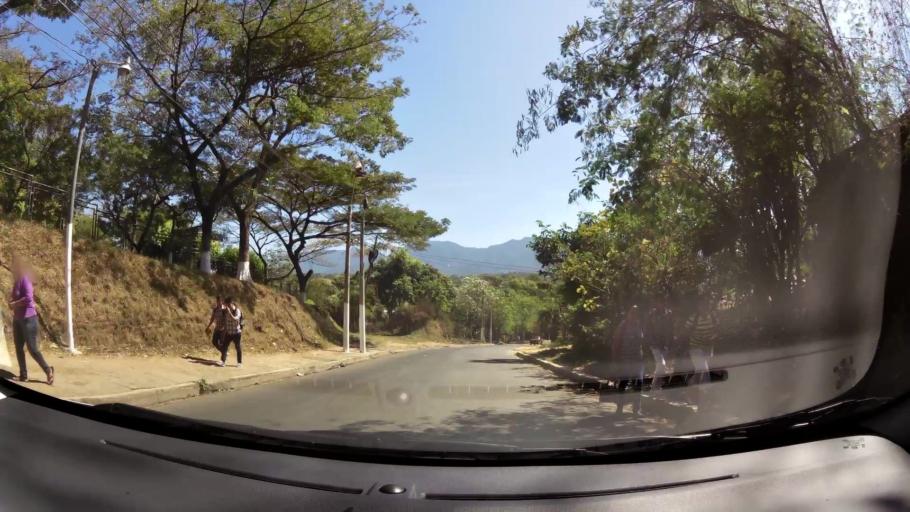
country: SV
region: Ahuachapan
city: Ahuachapan
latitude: 13.9361
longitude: -89.8570
